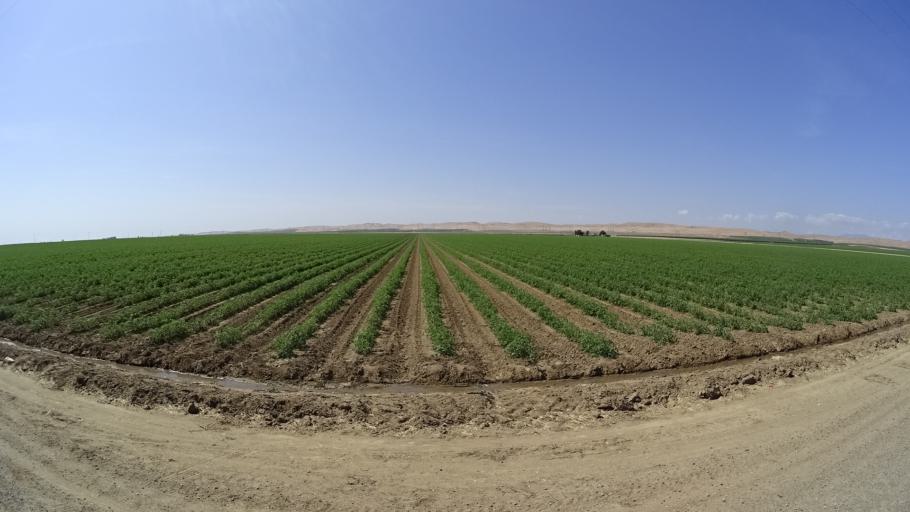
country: US
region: California
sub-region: Kings County
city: Kettleman City
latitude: 36.0725
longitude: -120.0355
